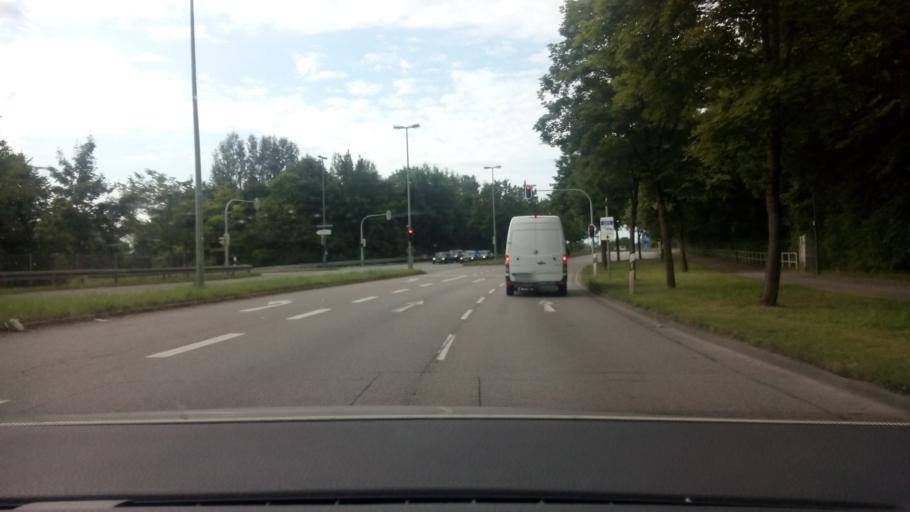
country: DE
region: Bavaria
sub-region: Upper Bavaria
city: Karlsfeld
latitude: 48.2123
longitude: 11.4847
